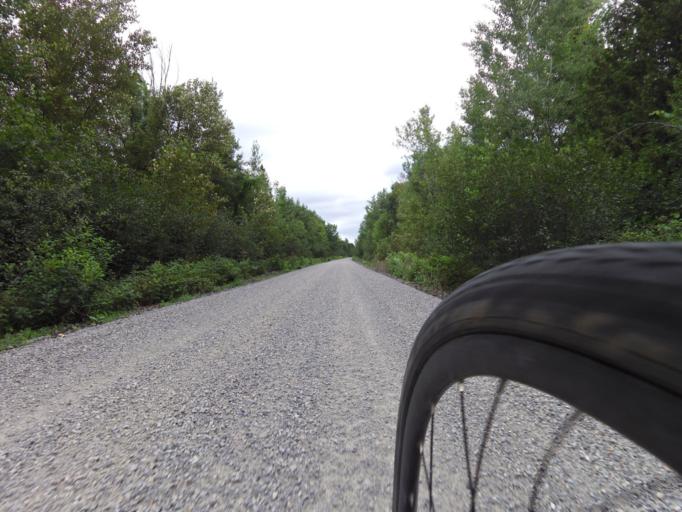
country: CA
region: Ontario
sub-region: Lanark County
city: Smiths Falls
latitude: 44.9621
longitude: -76.0513
